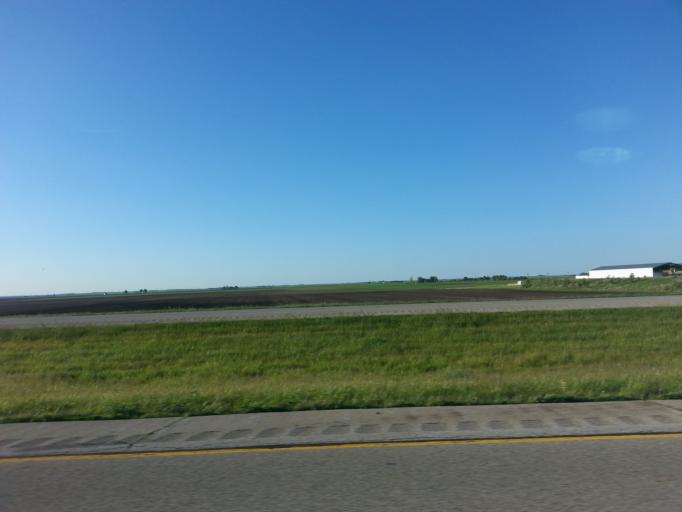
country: US
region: Illinois
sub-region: De Witt County
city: Farmer City
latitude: 40.2624
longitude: -88.6529
